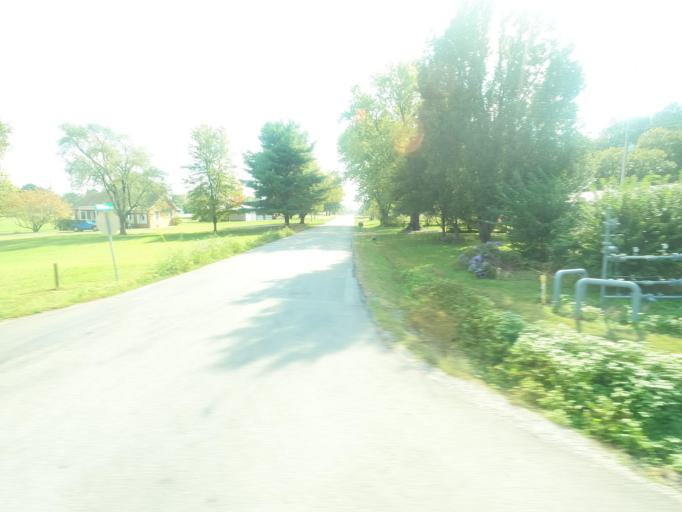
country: US
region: Illinois
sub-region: Massac County
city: Metropolis
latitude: 37.1913
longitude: -88.7199
